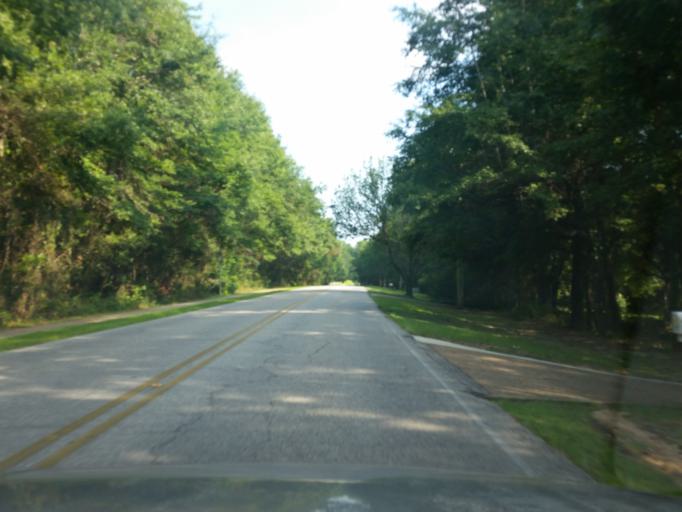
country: US
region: Alabama
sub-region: Baldwin County
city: Fairhope
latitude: 30.5494
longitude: -87.8975
